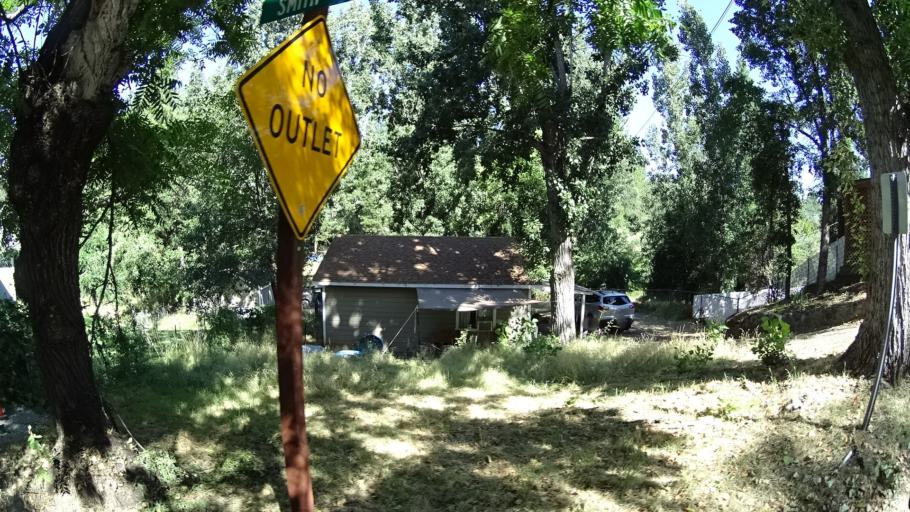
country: US
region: California
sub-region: Amador County
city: Pioneer
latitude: 38.3998
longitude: -120.5301
